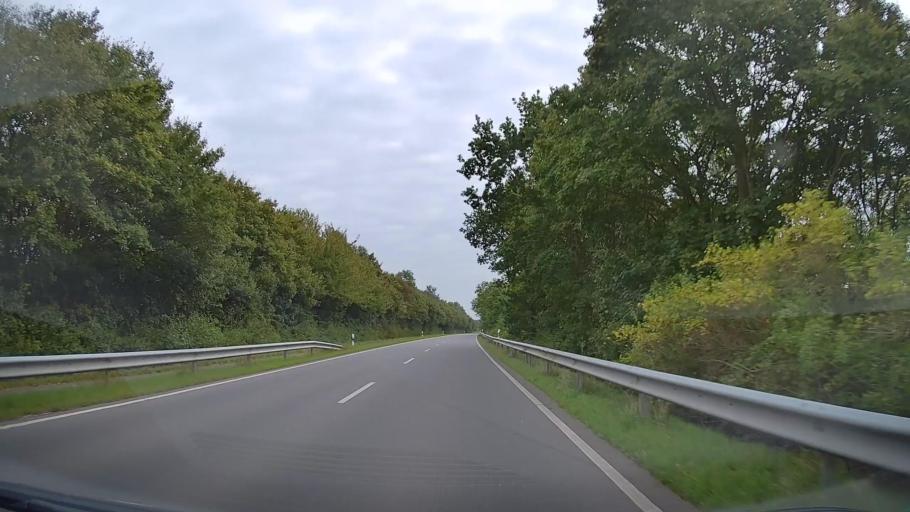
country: DE
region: Schleswig-Holstein
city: Krummbek
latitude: 54.4015
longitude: 10.3992
